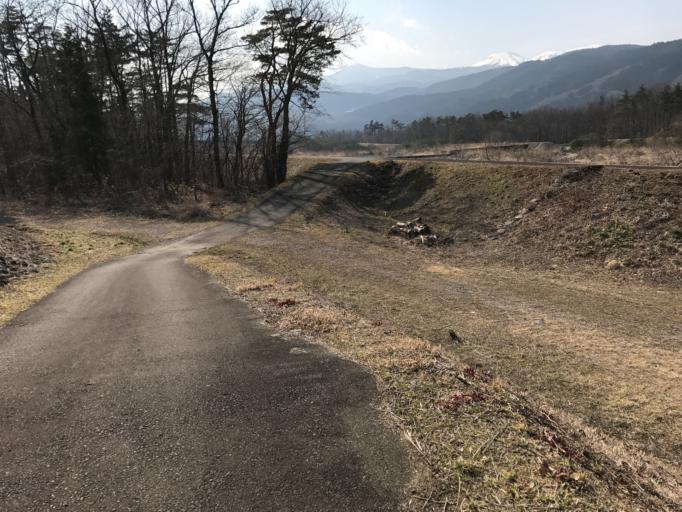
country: JP
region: Fukushima
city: Fukushima-shi
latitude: 37.7195
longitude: 140.3662
